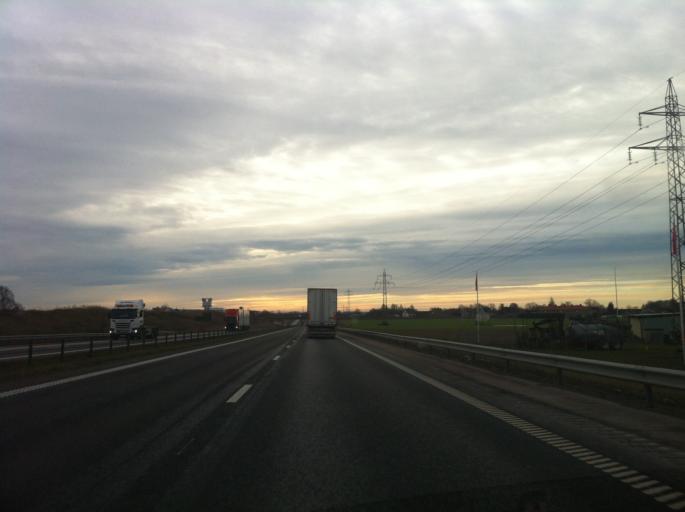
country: SE
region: Skane
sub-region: Astorps Kommun
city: Astorp
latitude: 56.1324
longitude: 12.9184
